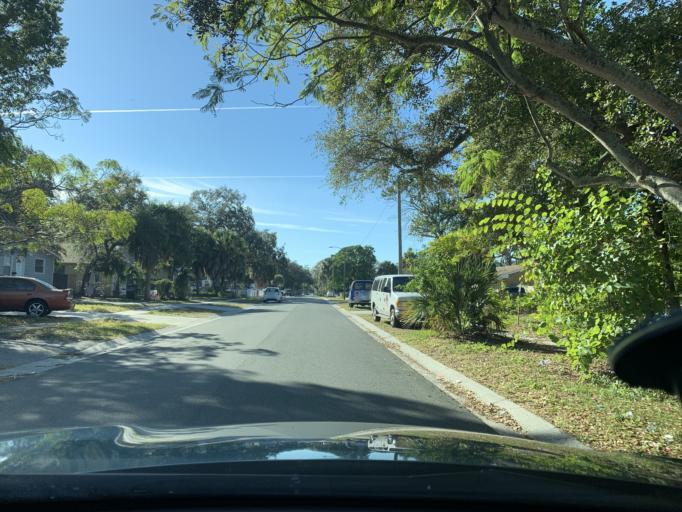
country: US
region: Florida
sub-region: Pinellas County
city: Gulfport
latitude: 27.7515
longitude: -82.6931
